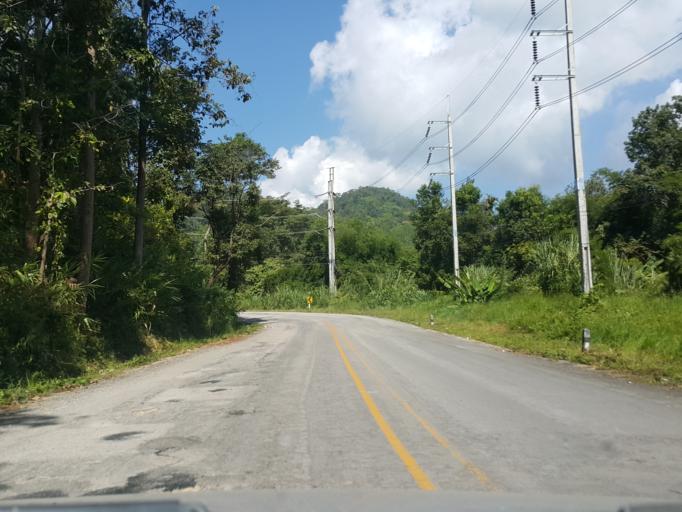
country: TH
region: Chiang Mai
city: Mae Taeng
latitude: 19.1238
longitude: 98.7695
